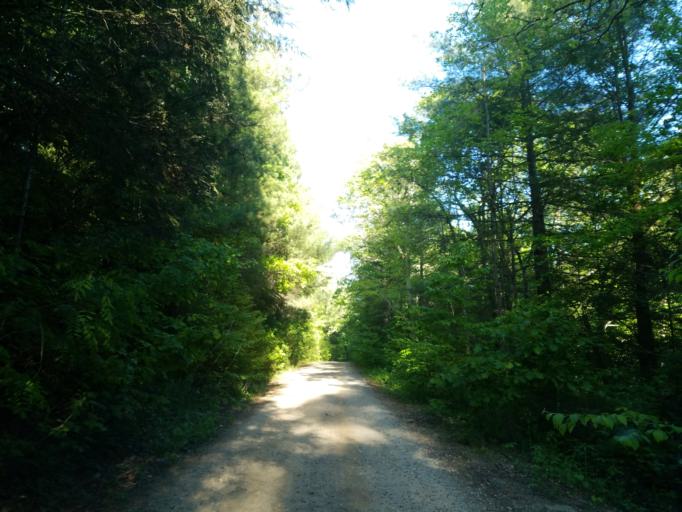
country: US
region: Georgia
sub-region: Lumpkin County
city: Dahlonega
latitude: 34.6804
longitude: -84.1362
